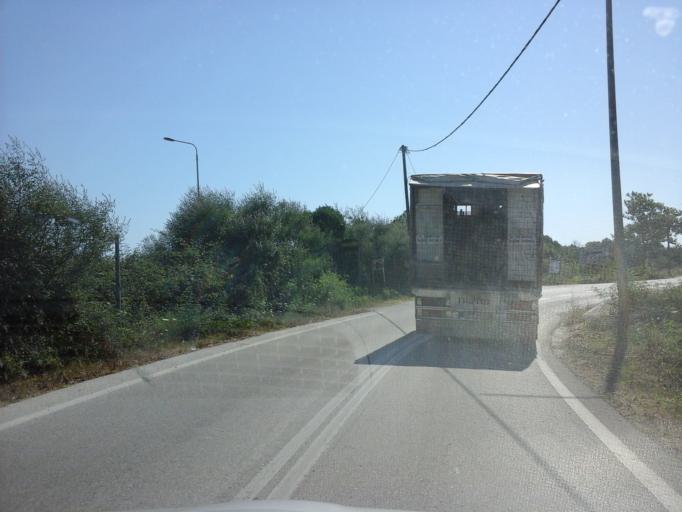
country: GR
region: East Macedonia and Thrace
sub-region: Nomos Evrou
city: Samothraki
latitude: 40.5029
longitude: 25.6029
